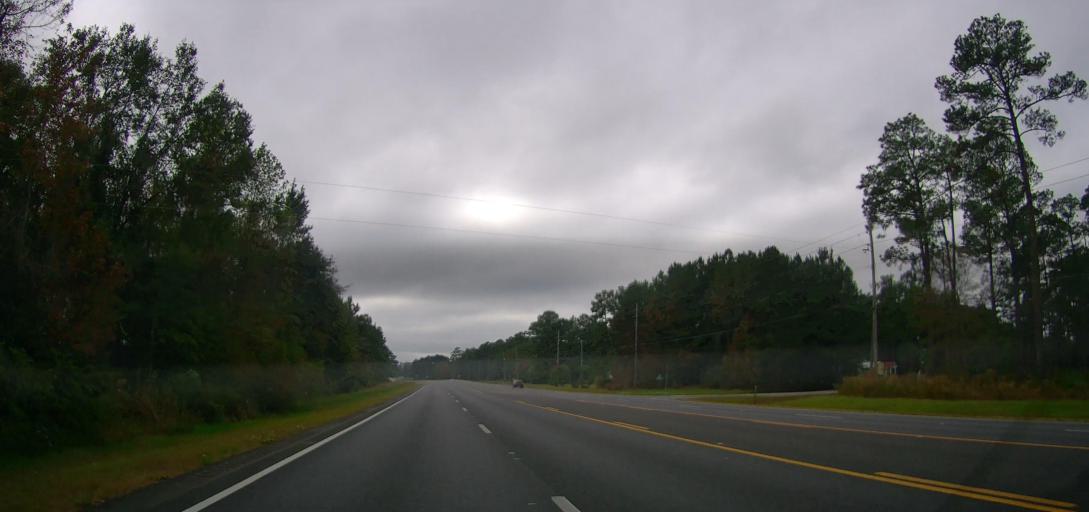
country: US
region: Georgia
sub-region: Thomas County
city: Thomasville
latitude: 30.8987
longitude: -83.9294
